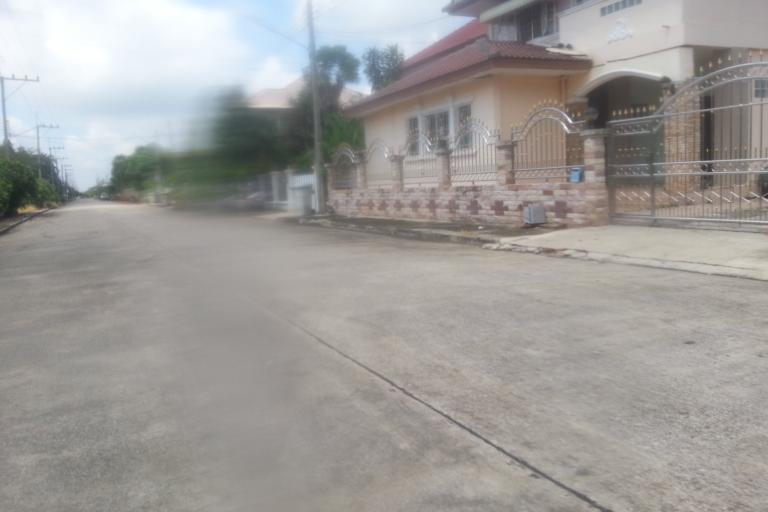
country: TH
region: Pathum Thani
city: Nong Suea
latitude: 14.0585
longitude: 100.8603
